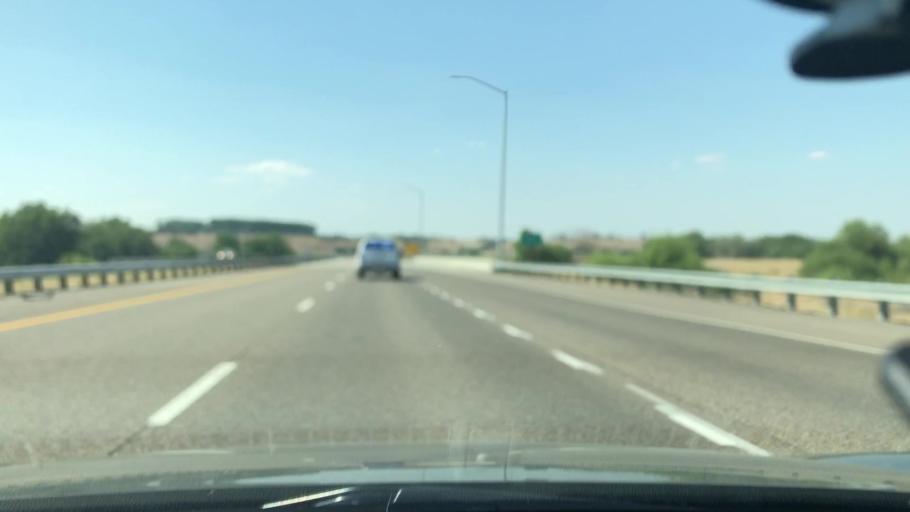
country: US
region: Oregon
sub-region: Malheur County
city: Ontario
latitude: 44.0525
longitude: -116.9812
